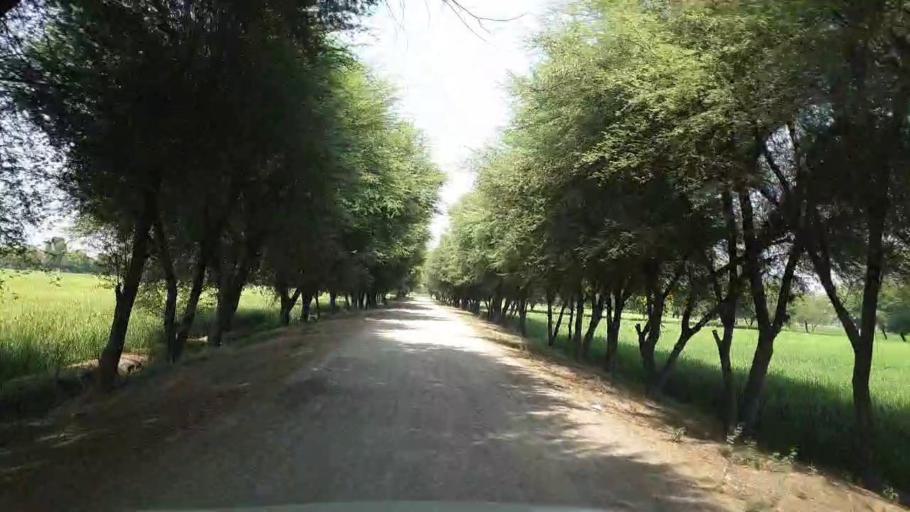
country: PK
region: Sindh
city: Dhoro Naro
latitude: 25.4828
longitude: 69.6221
